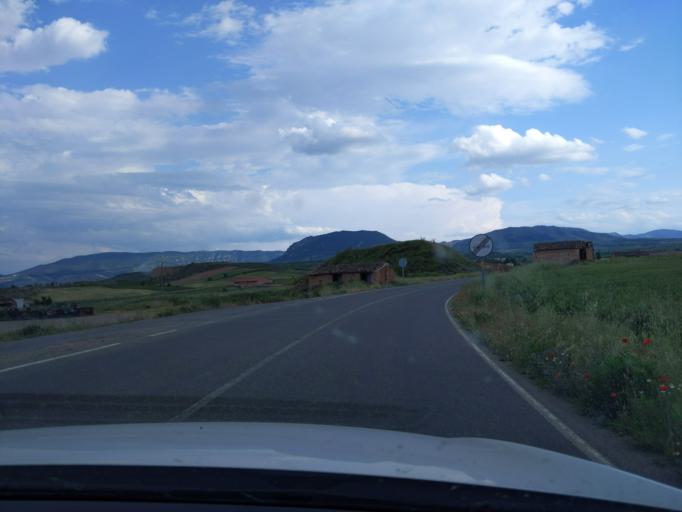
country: ES
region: La Rioja
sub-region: Provincia de La Rioja
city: Alberite
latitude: 42.4029
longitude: -2.4254
